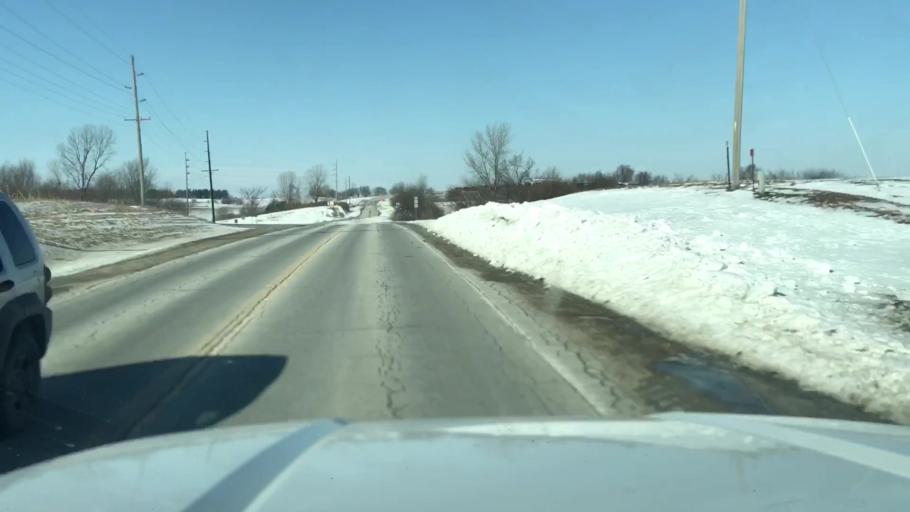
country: US
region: Missouri
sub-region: Andrew County
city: Savannah
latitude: 39.9609
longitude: -94.8561
